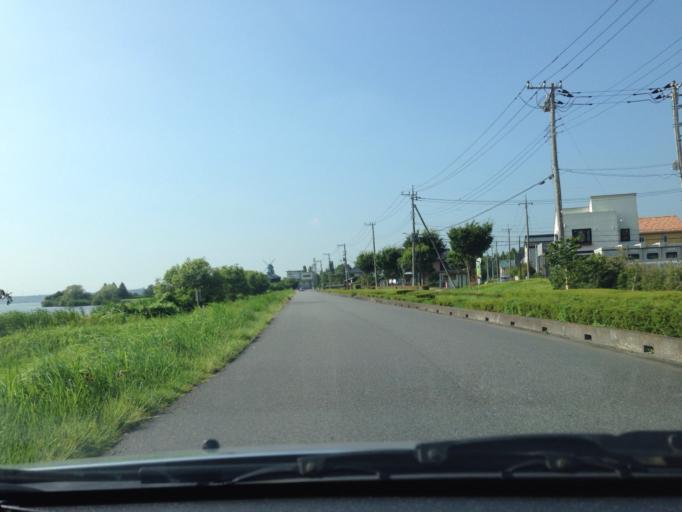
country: JP
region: Ibaraki
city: Ami
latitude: 36.0691
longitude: 140.2195
